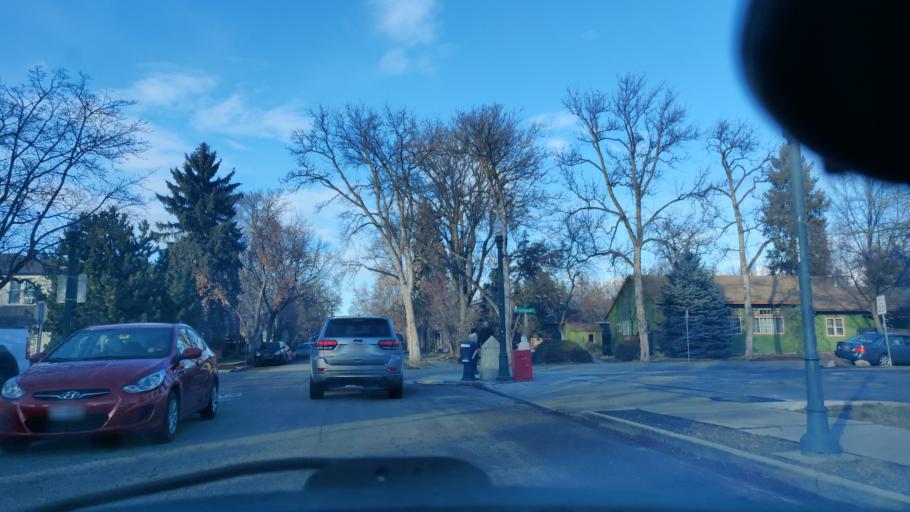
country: US
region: Idaho
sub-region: Ada County
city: Boise
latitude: 43.6308
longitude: -116.2034
